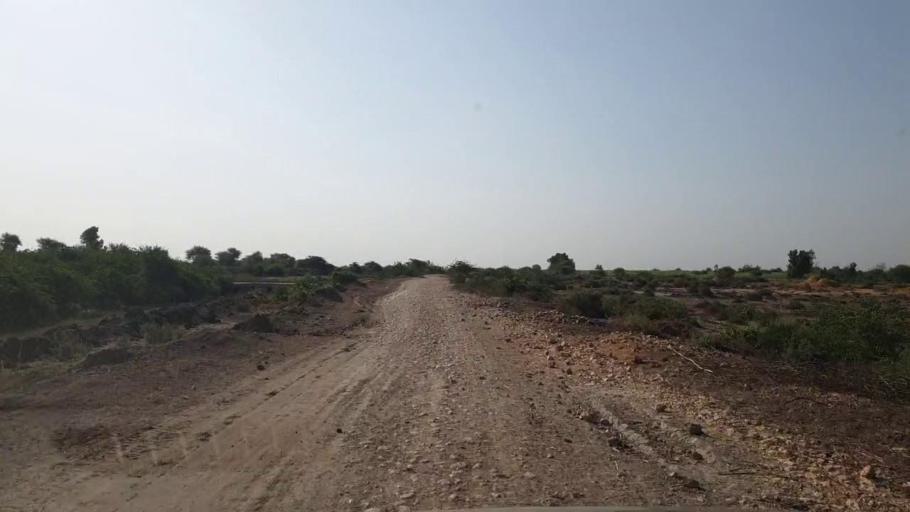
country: PK
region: Sindh
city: Kadhan
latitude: 24.6205
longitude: 69.0732
